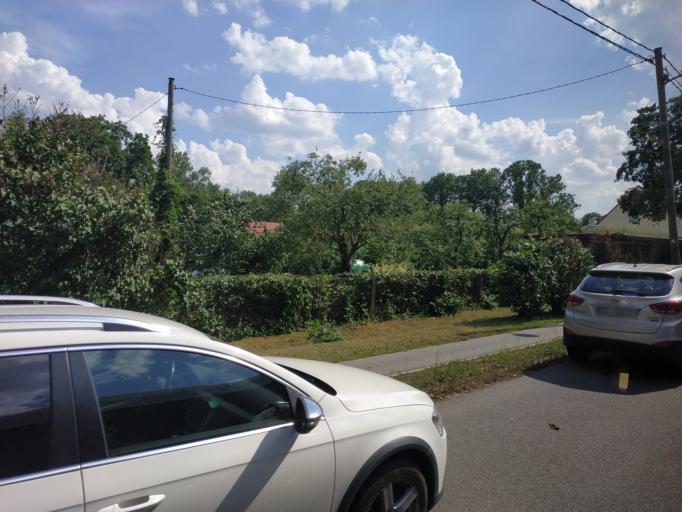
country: LV
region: Marupe
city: Marupe
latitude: 56.9317
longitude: 24.0245
